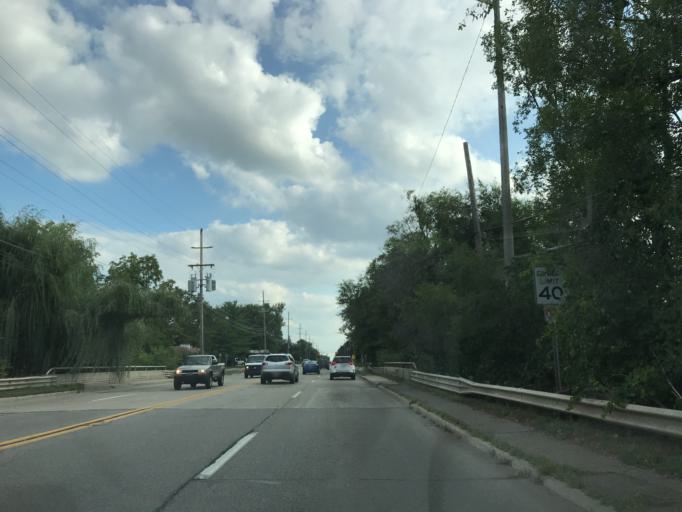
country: US
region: Michigan
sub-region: Wayne County
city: Redford
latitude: 42.3928
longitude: -83.2957
